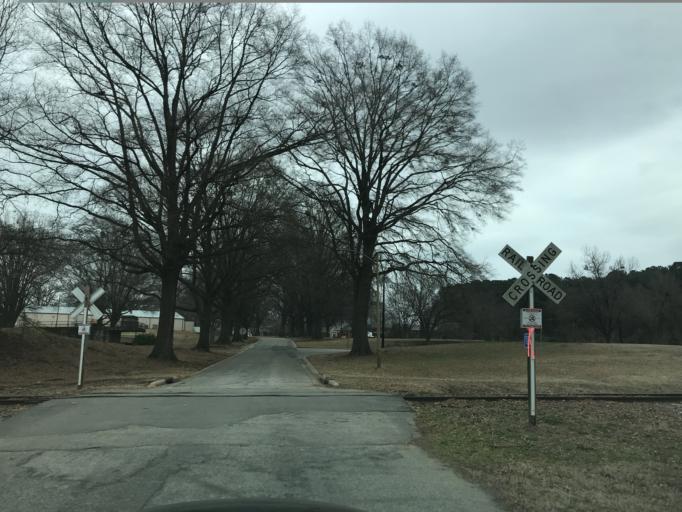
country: US
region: North Carolina
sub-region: Wake County
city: West Raleigh
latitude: 35.7664
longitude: -78.6601
